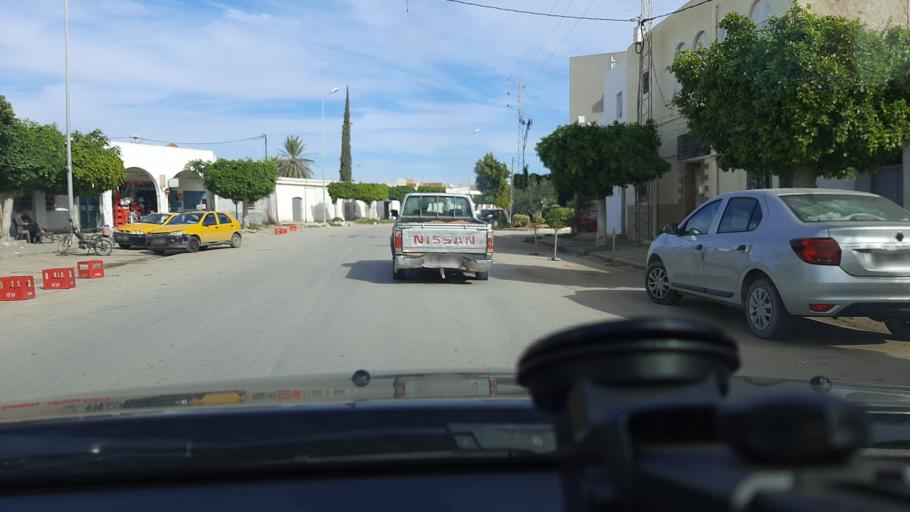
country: TN
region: Safaqis
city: Sfax
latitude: 34.7669
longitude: 10.7327
